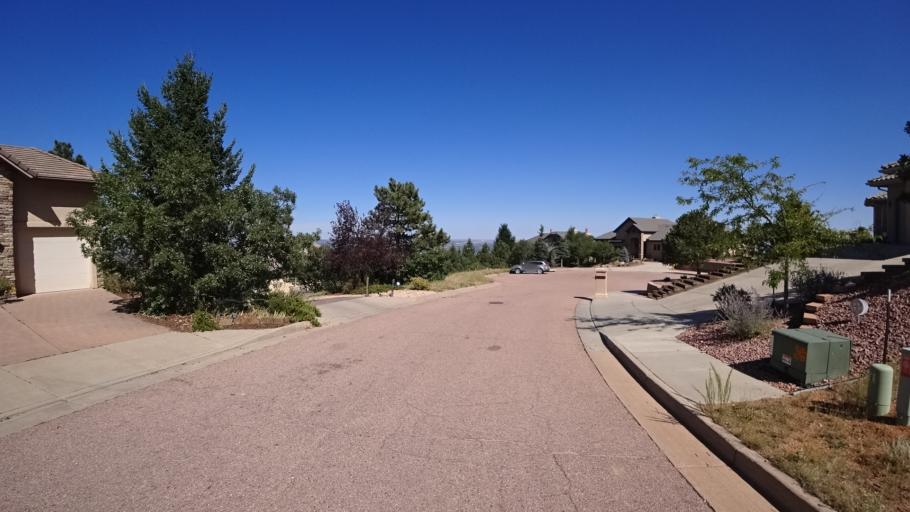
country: US
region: Colorado
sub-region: El Paso County
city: Manitou Springs
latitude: 38.8143
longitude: -104.8795
